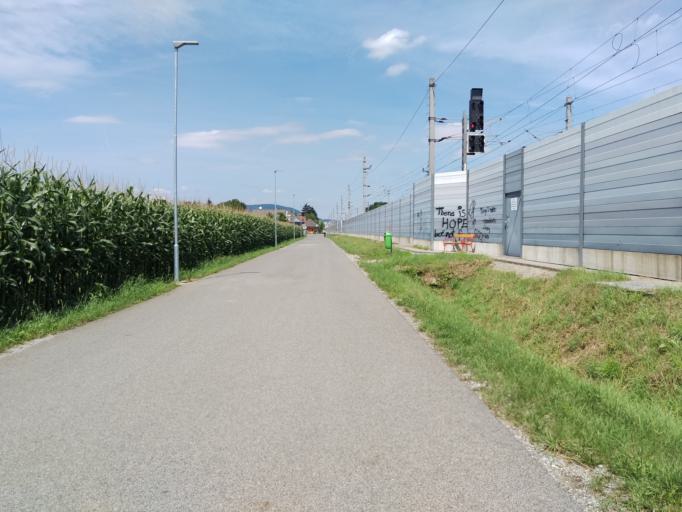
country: AT
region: Styria
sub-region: Politischer Bezirk Graz-Umgebung
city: Feldkirchen bei Graz
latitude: 47.0191
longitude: 15.4361
